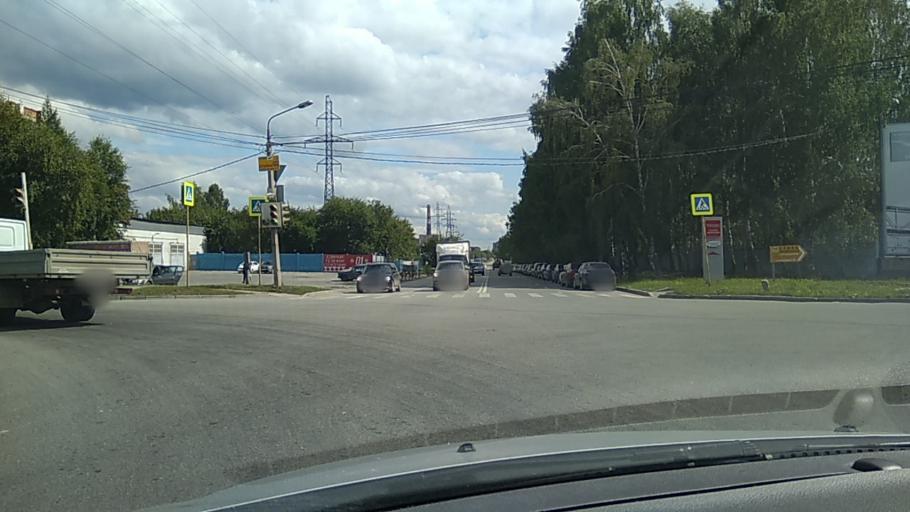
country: RU
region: Sverdlovsk
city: Shuvakish
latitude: 56.8848
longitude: 60.5327
